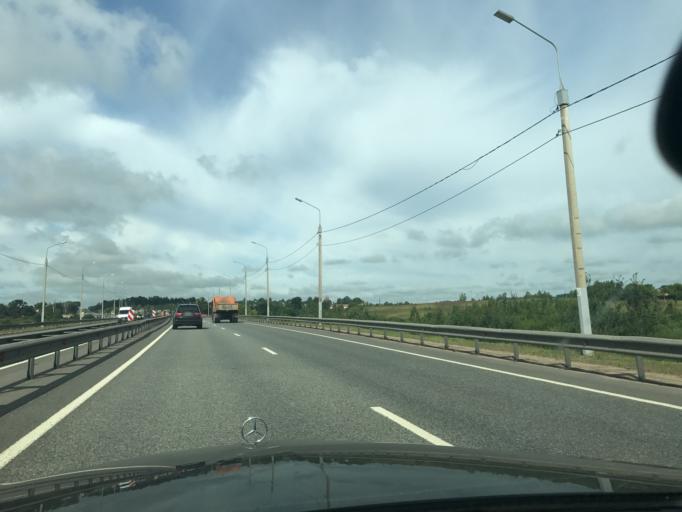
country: RU
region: Smolensk
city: Yartsevo
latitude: 55.0791
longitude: 32.6824
